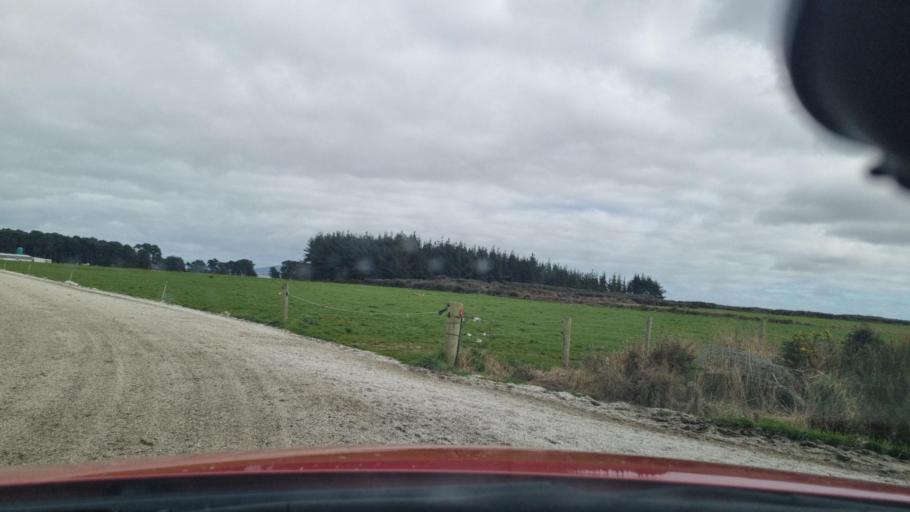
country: NZ
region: Southland
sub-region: Invercargill City
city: Bluff
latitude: -46.5615
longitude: 168.4914
